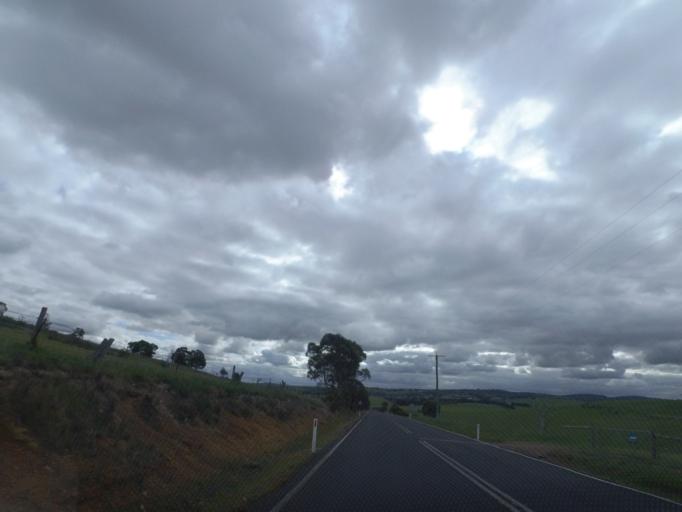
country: AU
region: Victoria
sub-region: Whittlesea
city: Whittlesea
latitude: -37.5246
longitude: 145.1056
